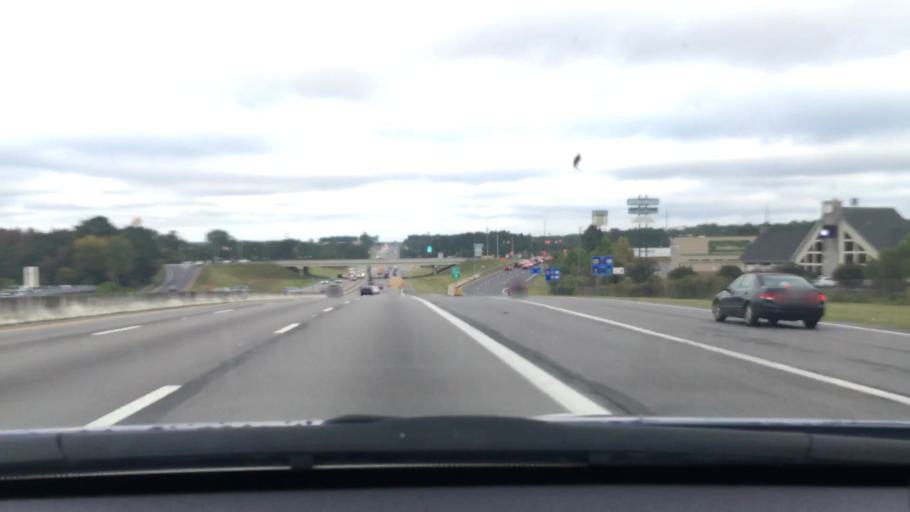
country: US
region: South Carolina
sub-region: Lexington County
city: Seven Oaks
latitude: 34.0650
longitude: -81.1395
